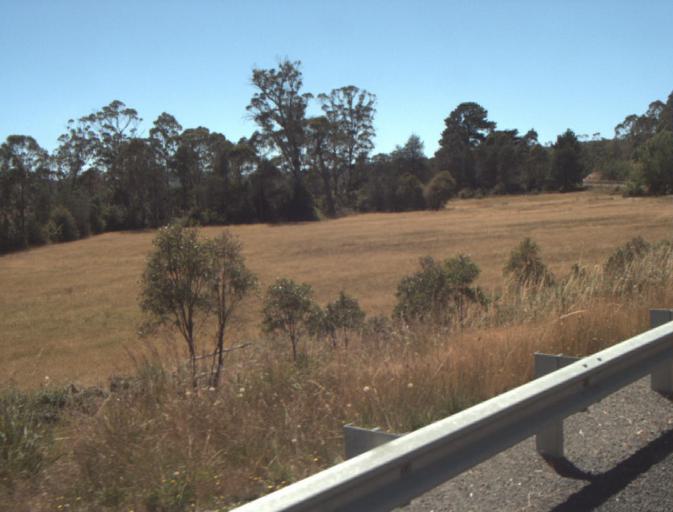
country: AU
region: Tasmania
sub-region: Launceston
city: Newstead
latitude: -41.3711
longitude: 147.3193
